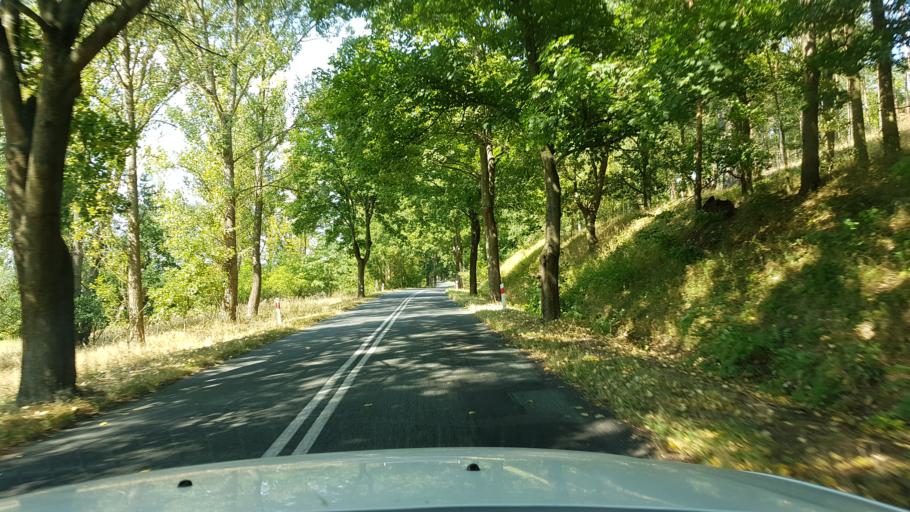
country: PL
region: West Pomeranian Voivodeship
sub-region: Powiat gryfinski
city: Cedynia
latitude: 52.8228
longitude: 14.2280
